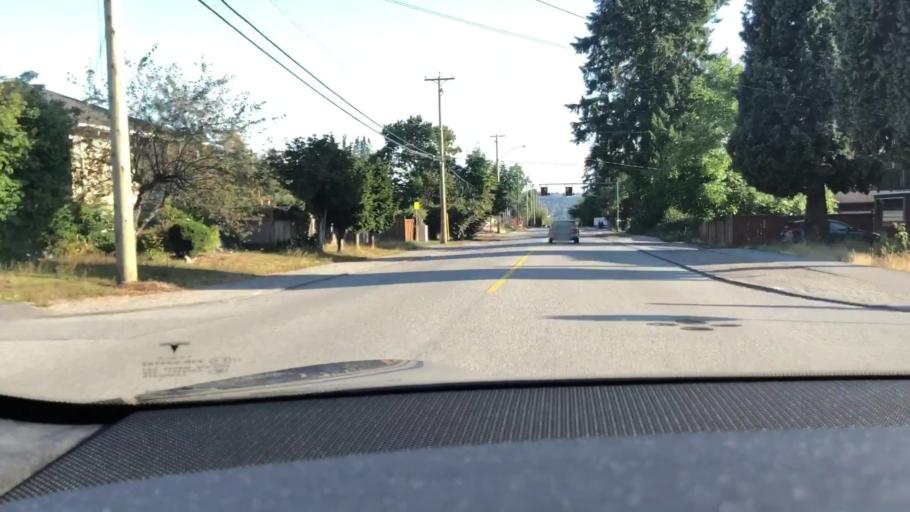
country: CA
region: British Columbia
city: Burnaby
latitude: 49.2725
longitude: -122.9701
